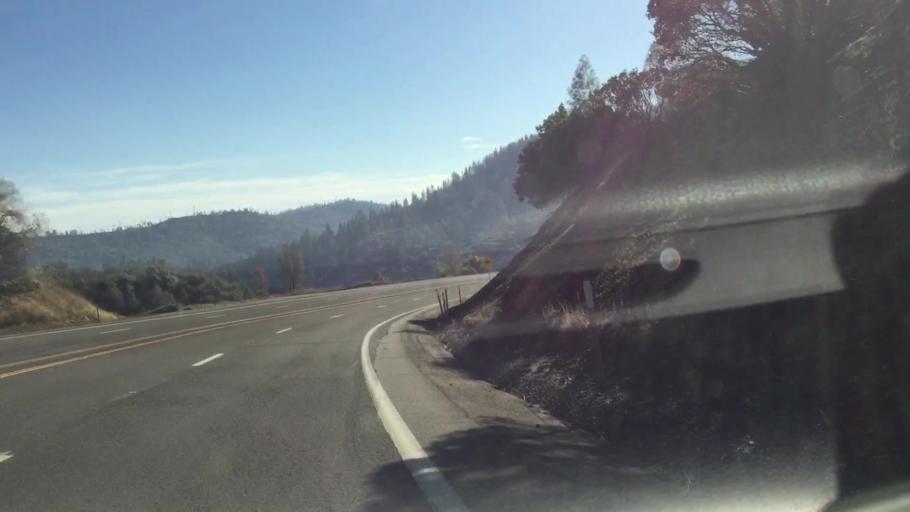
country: US
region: California
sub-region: Butte County
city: Berry Creek
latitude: 39.6713
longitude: -121.5263
